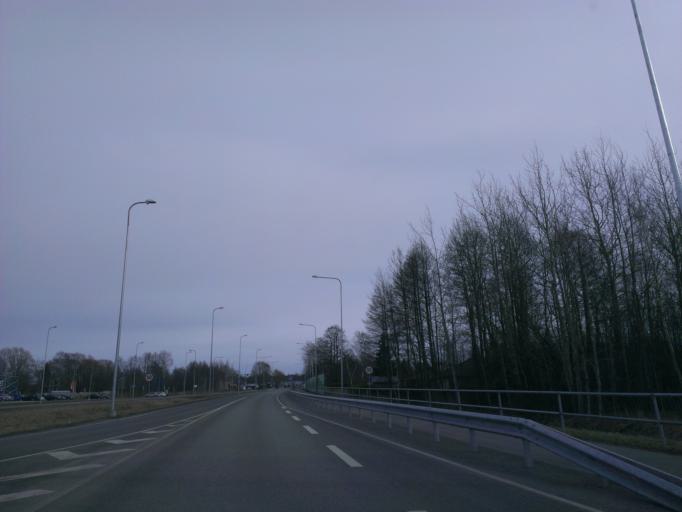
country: EE
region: Paernumaa
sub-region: Paernu linn
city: Parnu
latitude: 58.3955
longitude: 24.4546
